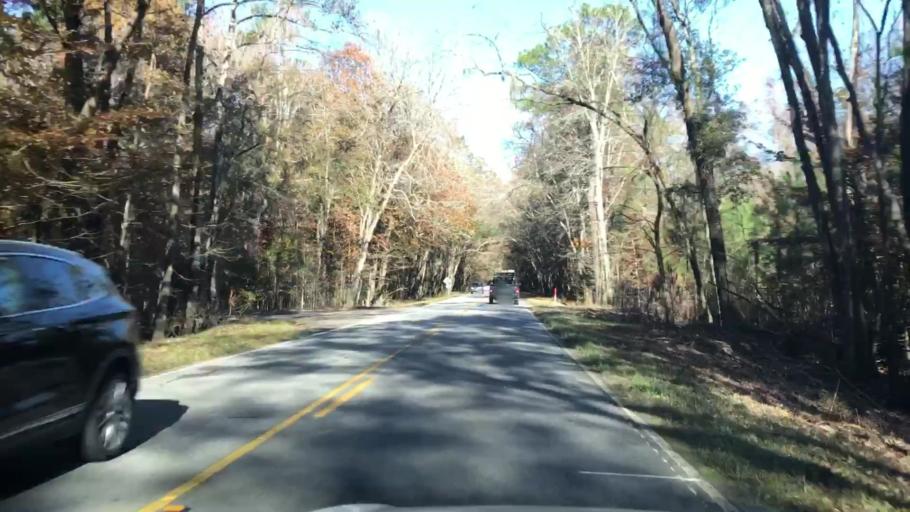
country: US
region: South Carolina
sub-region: Berkeley County
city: Ladson
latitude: 32.9056
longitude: -80.1468
